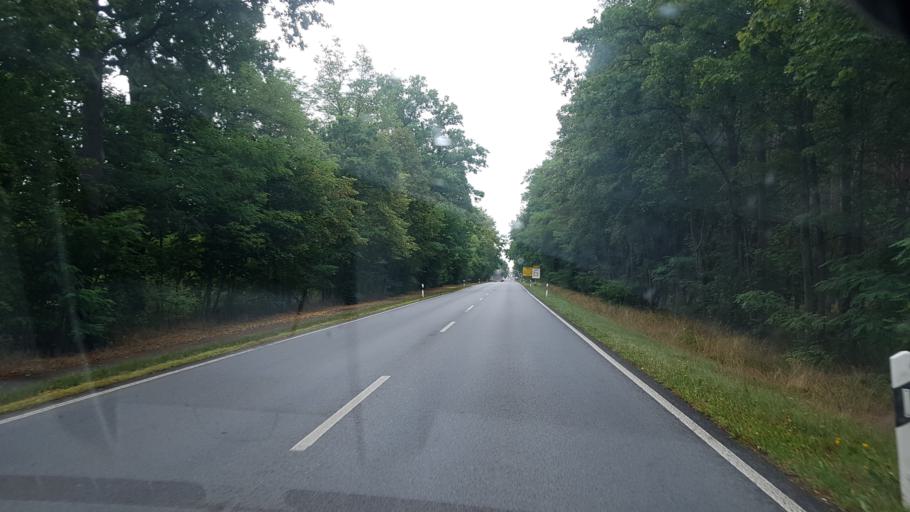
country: DE
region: Saxony
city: Niesky
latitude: 51.2756
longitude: 14.8176
